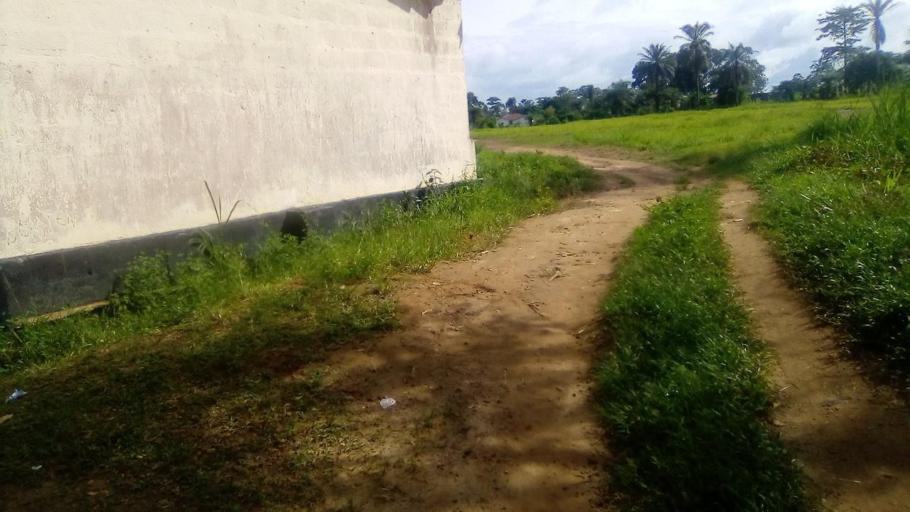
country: SL
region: Southern Province
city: Pujehun
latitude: 7.3607
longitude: -11.7288
